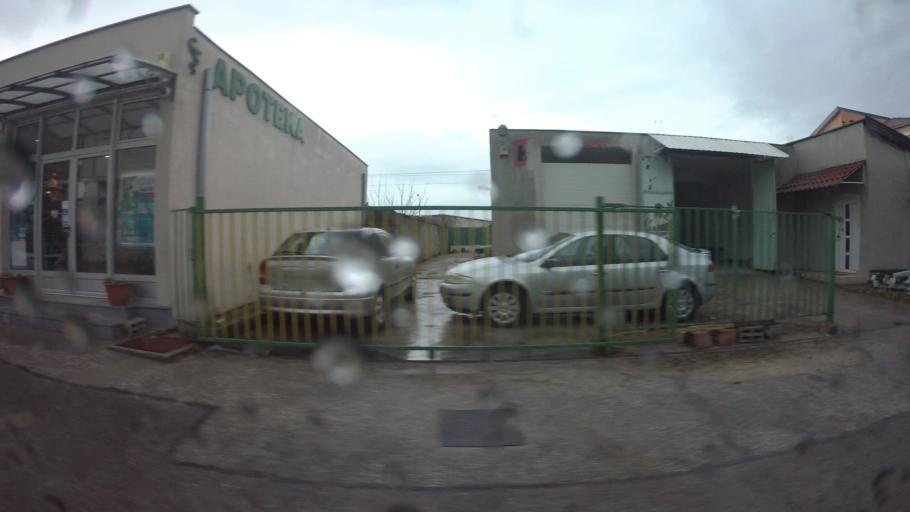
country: BA
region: Federation of Bosnia and Herzegovina
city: Rodoc
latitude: 43.3235
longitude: 17.8305
